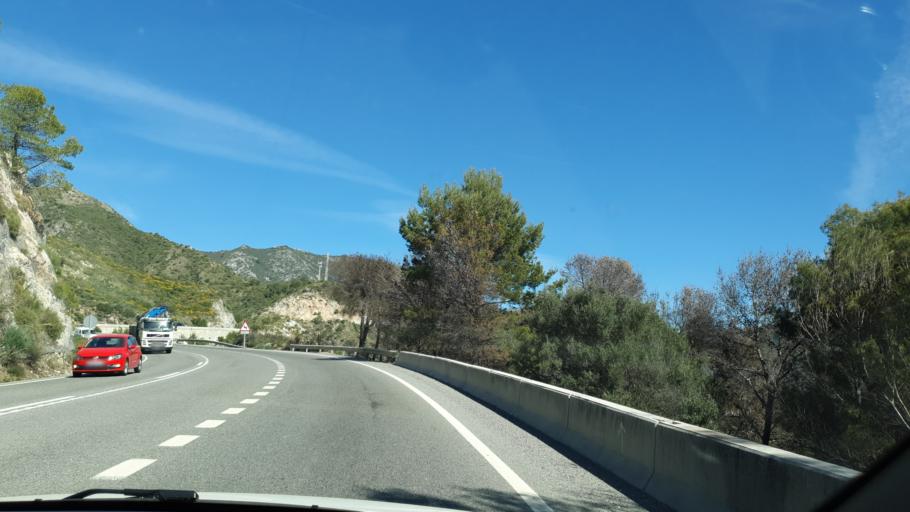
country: ES
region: Andalusia
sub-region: Provincia de Malaga
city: Ojen
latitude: 36.5512
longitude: -4.8615
